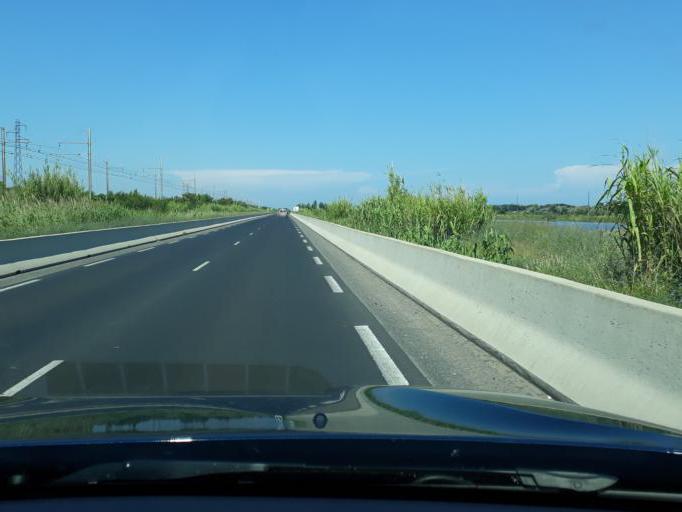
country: FR
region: Languedoc-Roussillon
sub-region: Departement de l'Herault
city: Marseillan
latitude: 43.3260
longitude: 3.5522
